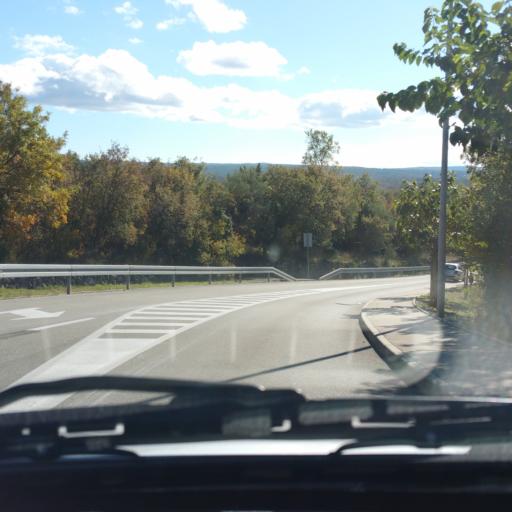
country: HR
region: Primorsko-Goranska
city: Omisalj
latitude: 45.2051
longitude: 14.5607
